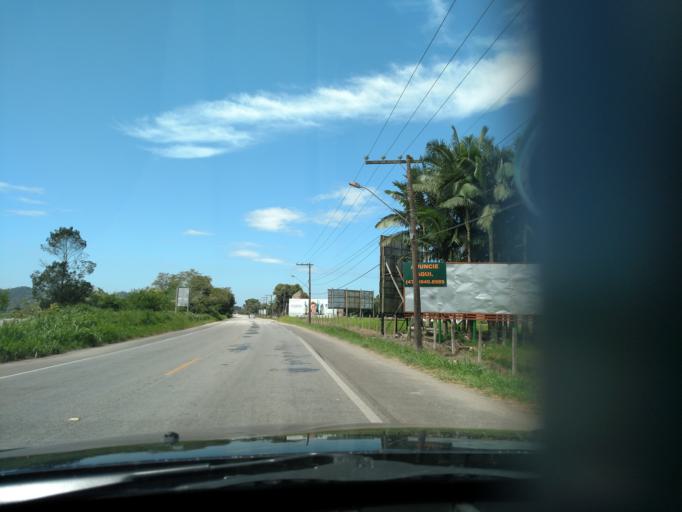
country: BR
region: Santa Catarina
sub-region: Itajai
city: Itajai
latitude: -26.8841
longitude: -48.8033
